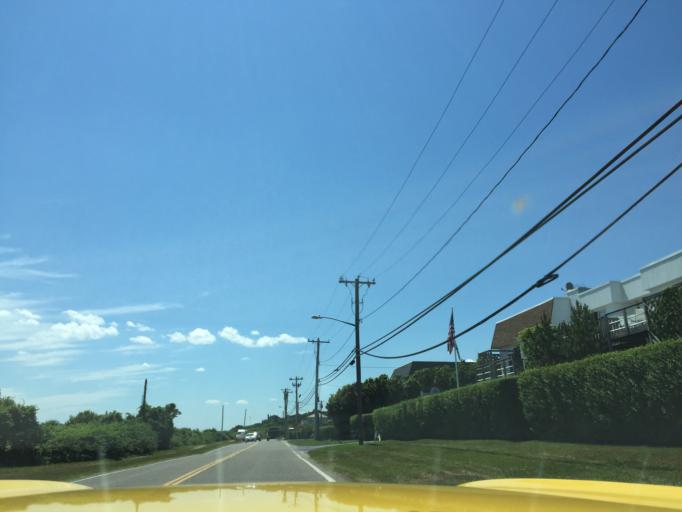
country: US
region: New York
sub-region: Suffolk County
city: Montauk
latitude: 41.0277
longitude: -71.9611
